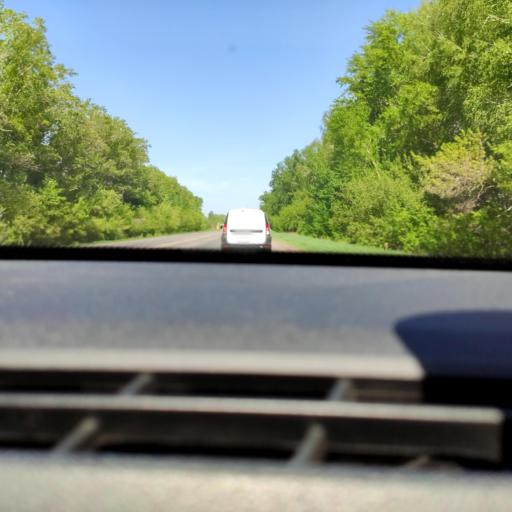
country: RU
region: Samara
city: Tol'yatti
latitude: 53.6283
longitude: 49.4167
